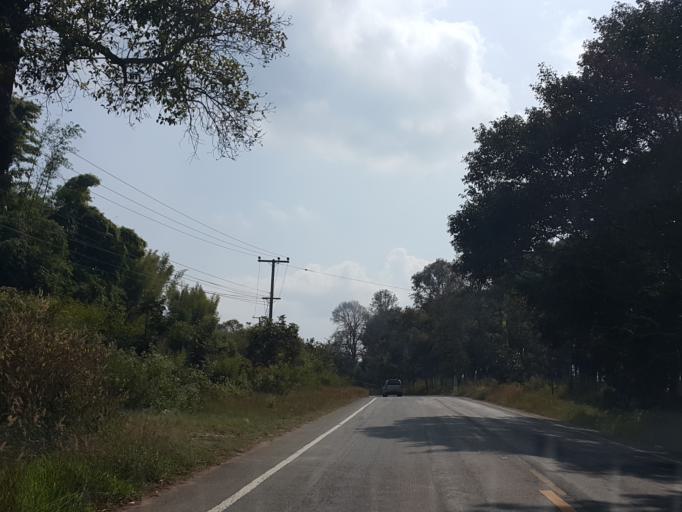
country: TH
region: Chiang Mai
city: Hot
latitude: 18.1158
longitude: 98.3782
